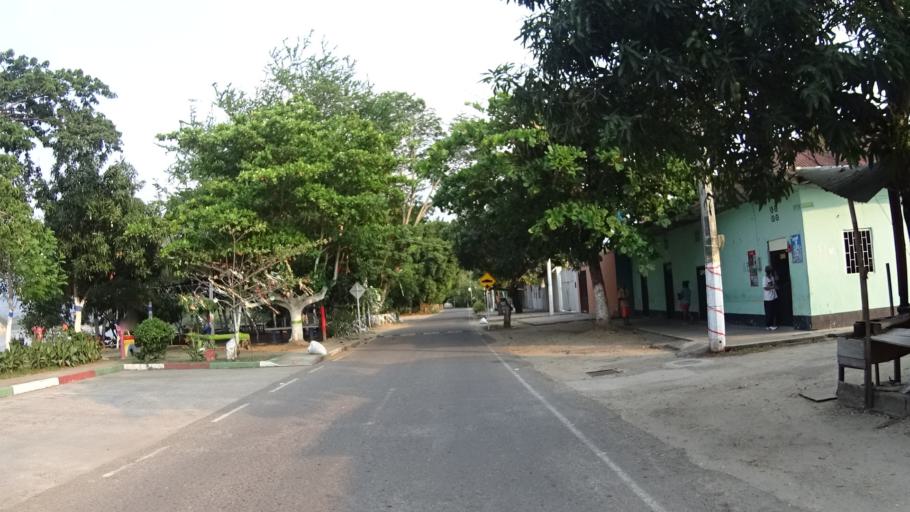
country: CO
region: Caldas
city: La Dorada
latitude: 5.4478
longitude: -74.6597
